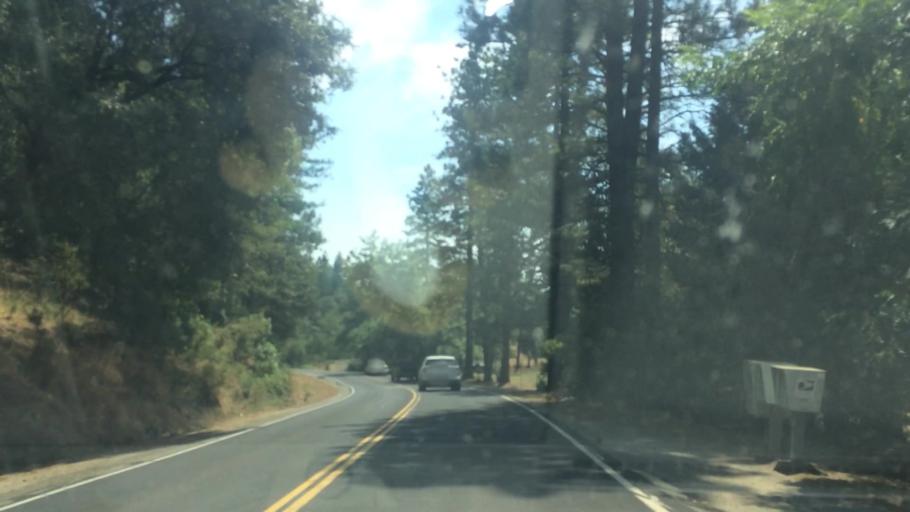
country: US
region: California
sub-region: Amador County
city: Pine Grove
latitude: 38.4147
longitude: -120.7001
